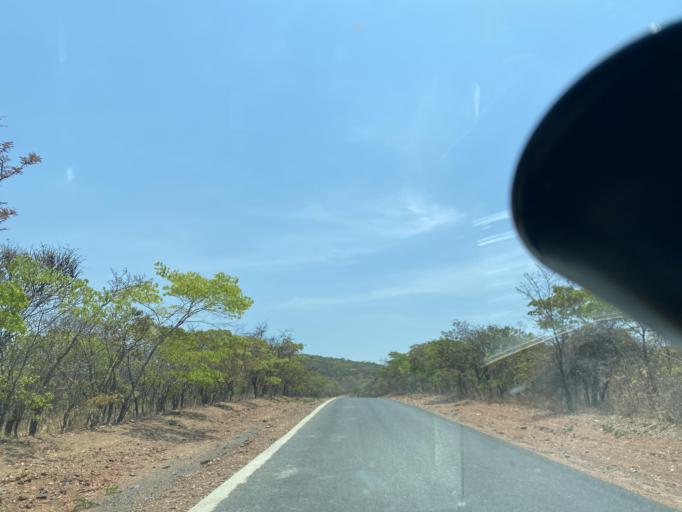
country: ZM
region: Lusaka
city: Kafue
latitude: -15.8633
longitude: 28.4269
